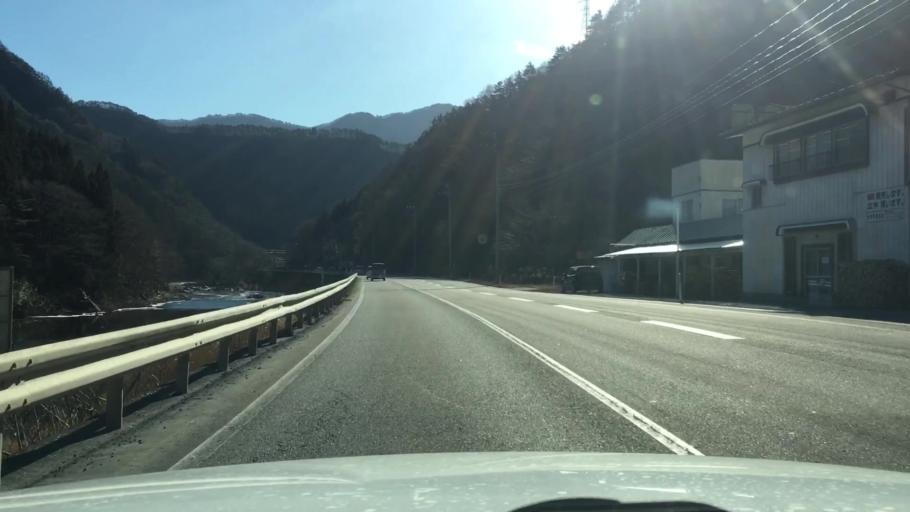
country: JP
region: Iwate
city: Miyako
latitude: 39.6151
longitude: 141.7888
